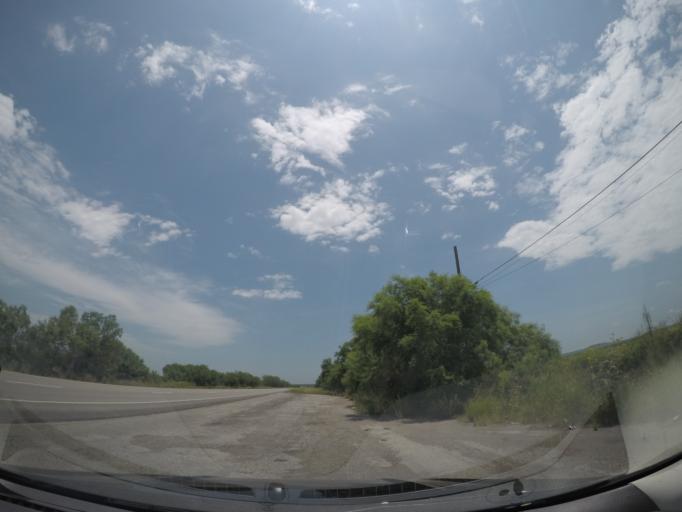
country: US
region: Texas
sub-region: Uvalde County
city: Uvalde Estates
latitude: 29.2340
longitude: -100.1192
